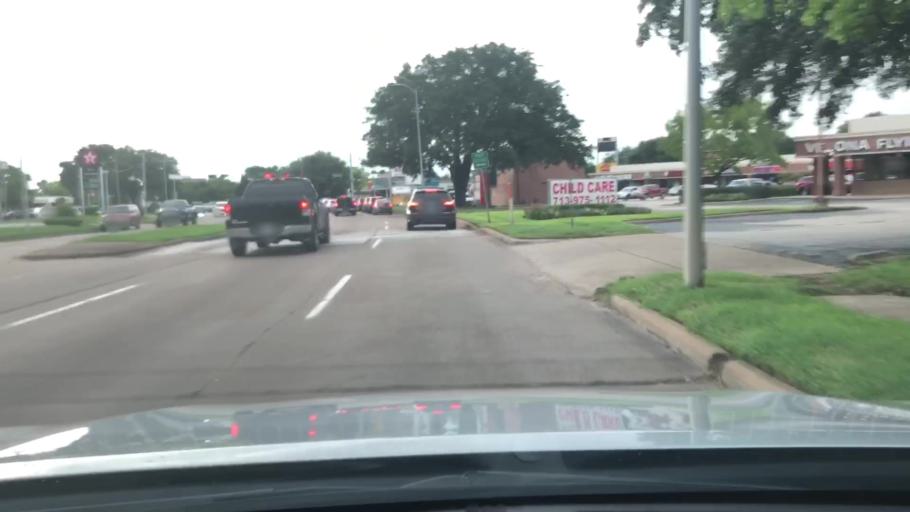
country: US
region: Texas
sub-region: Harris County
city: Piney Point Village
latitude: 29.7216
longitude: -95.5378
